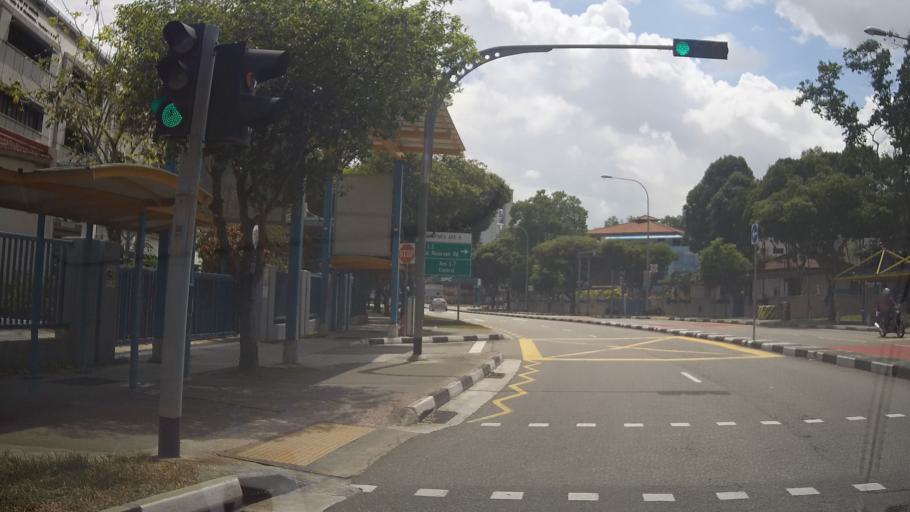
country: SG
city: Singapore
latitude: 1.3488
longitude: 103.9369
